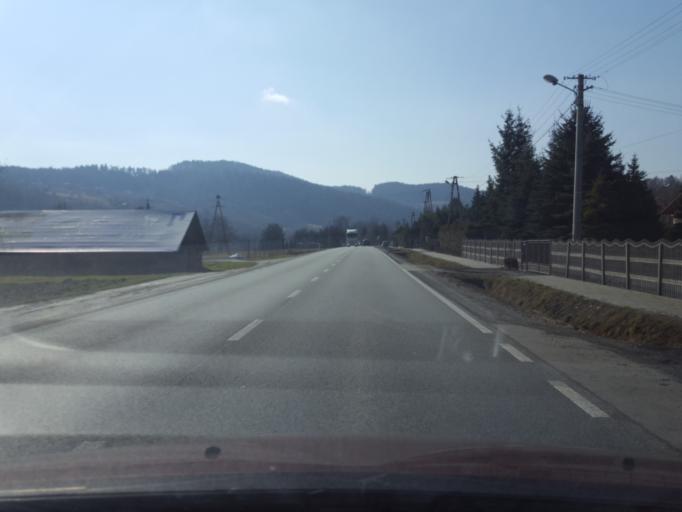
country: PL
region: Lesser Poland Voivodeship
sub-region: Powiat brzeski
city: Czchow
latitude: 49.8222
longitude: 20.6799
